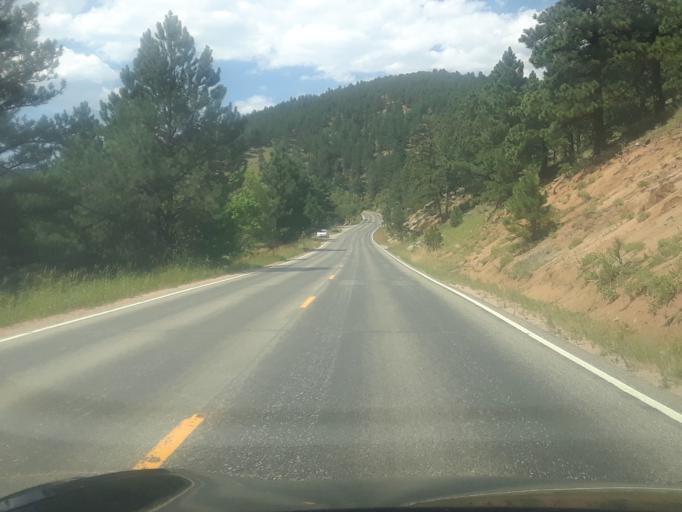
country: US
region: Colorado
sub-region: Boulder County
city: Boulder
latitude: 40.0330
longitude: -105.3236
